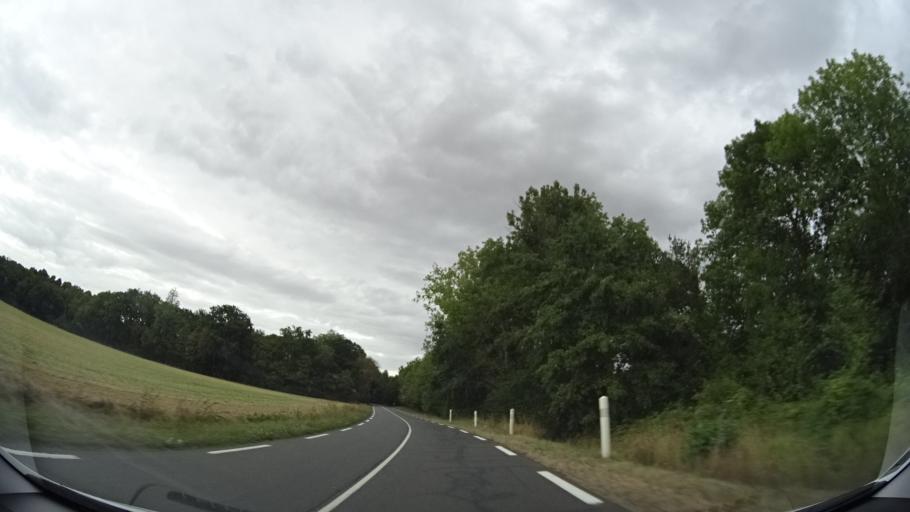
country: FR
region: Centre
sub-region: Departement du Loiret
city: Trigueres
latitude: 47.9362
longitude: 2.9625
